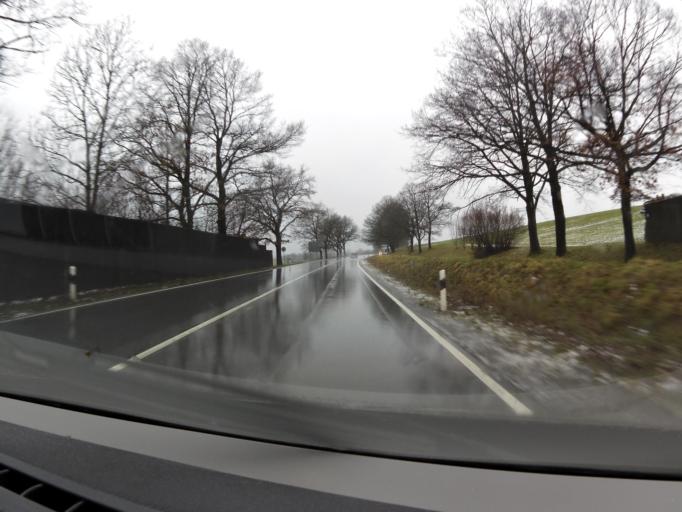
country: DE
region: Bavaria
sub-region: Upper Bavaria
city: Reichersbeuern
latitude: 47.7638
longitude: 11.6366
